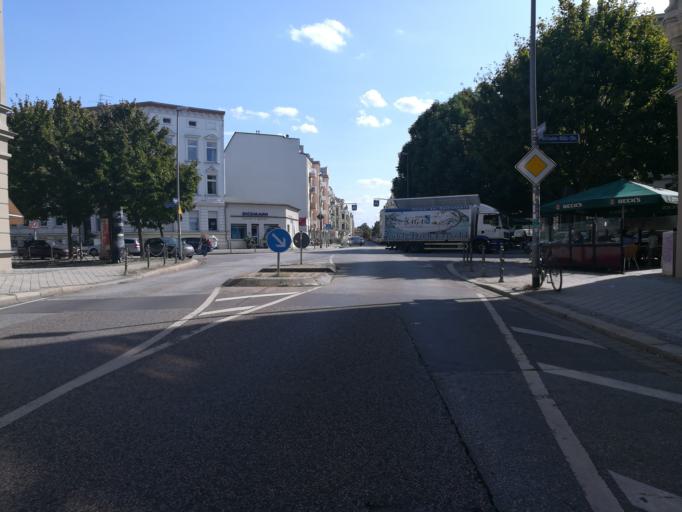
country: DE
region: Saxony-Anhalt
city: Magdeburg
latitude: 52.1271
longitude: 11.6122
